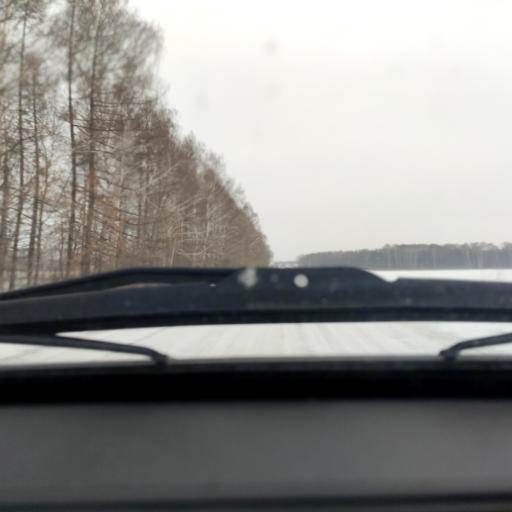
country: RU
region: Bashkortostan
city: Mikhaylovka
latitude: 54.8542
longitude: 55.8675
